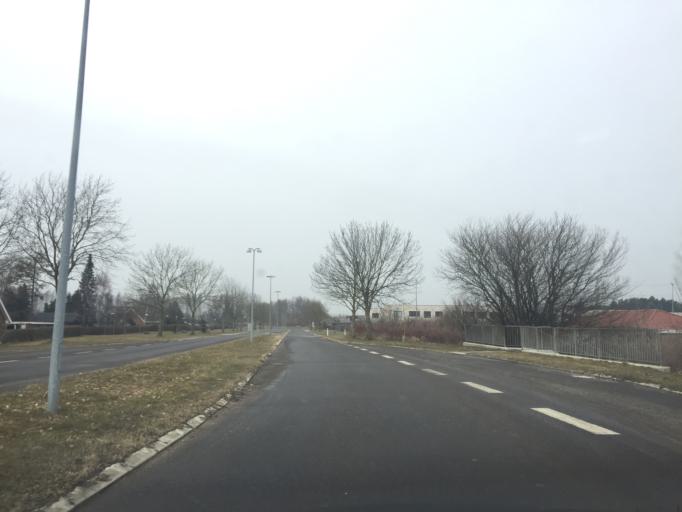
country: DK
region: Capital Region
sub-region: Hoje-Taastrup Kommune
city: Flong
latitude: 55.6475
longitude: 12.2291
